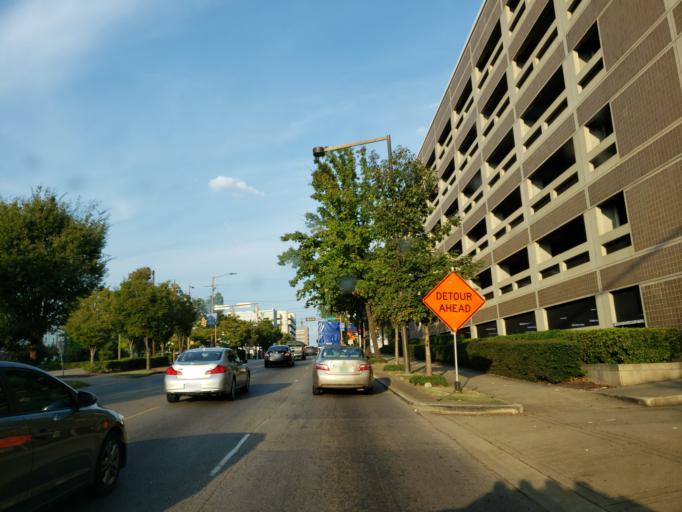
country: US
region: Alabama
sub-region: Jefferson County
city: Birmingham
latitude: 33.5198
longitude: -86.8141
